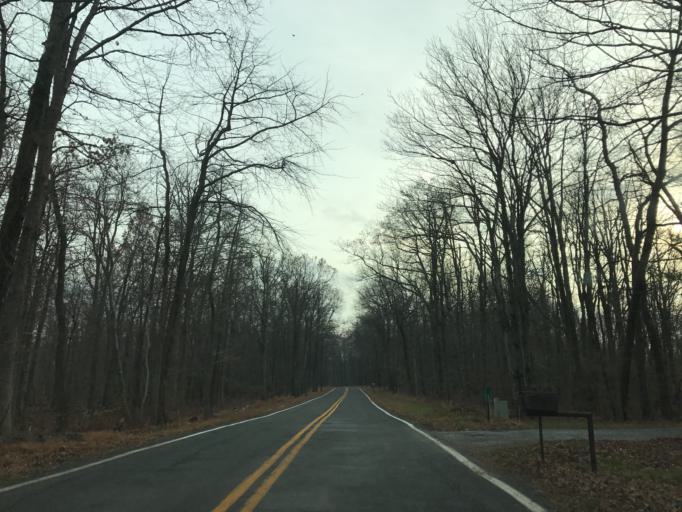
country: US
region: Maryland
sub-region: Frederick County
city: Myersville
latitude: 39.5609
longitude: -77.4989
